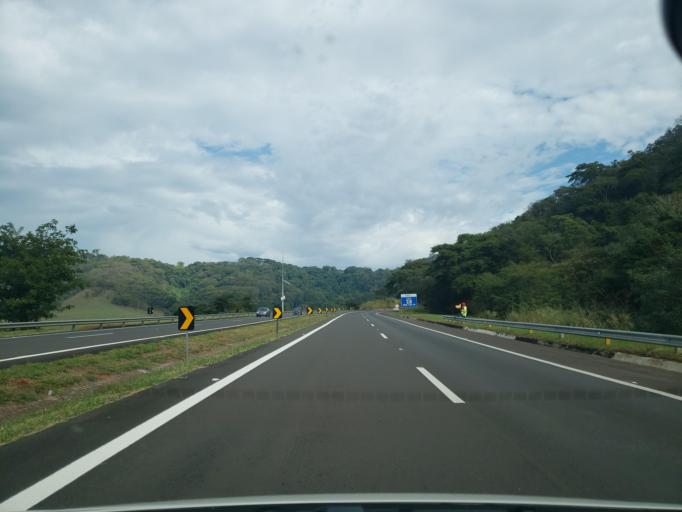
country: BR
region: Sao Paulo
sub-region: Dois Corregos
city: Dois Corregos
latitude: -22.2493
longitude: -48.3363
